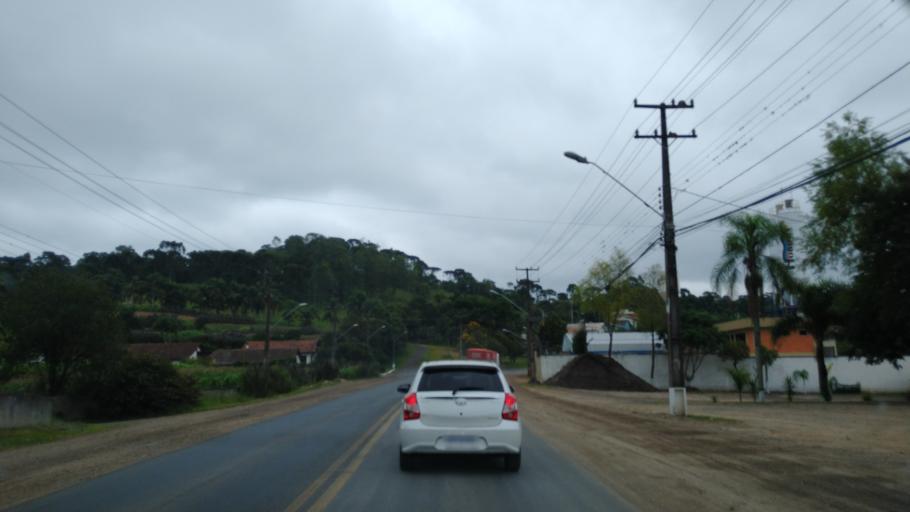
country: BR
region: Parana
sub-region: Uniao Da Vitoria
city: Uniao da Vitoria
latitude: -26.2514
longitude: -51.1160
